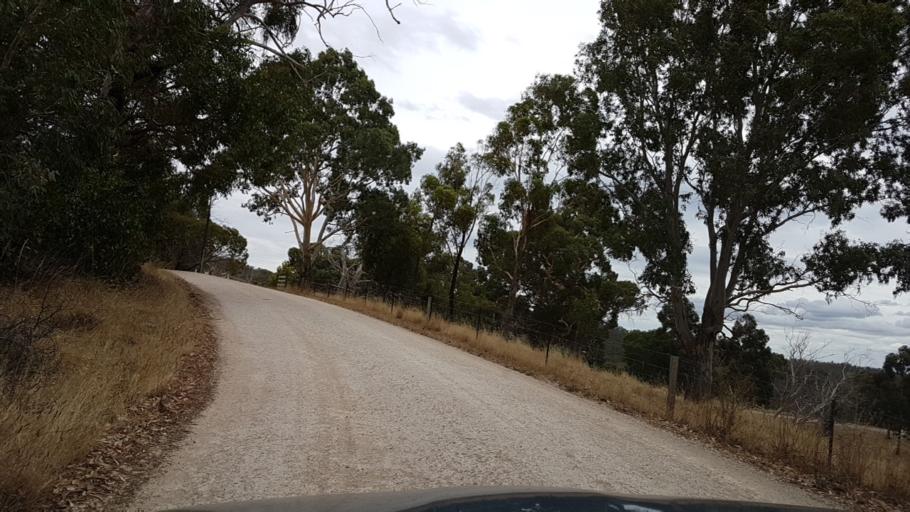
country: AU
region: South Australia
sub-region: Adelaide Hills
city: Gumeracha
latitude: -34.7983
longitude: 138.8179
